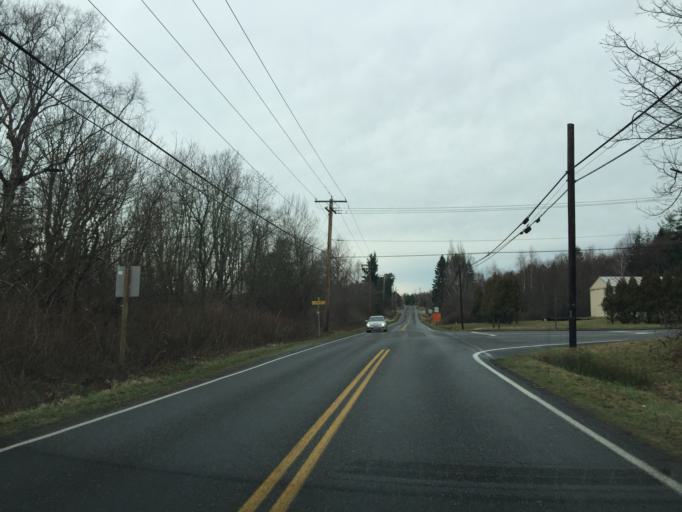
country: US
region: Washington
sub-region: Whatcom County
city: Marietta-Alderwood
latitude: 48.7789
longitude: -122.5387
